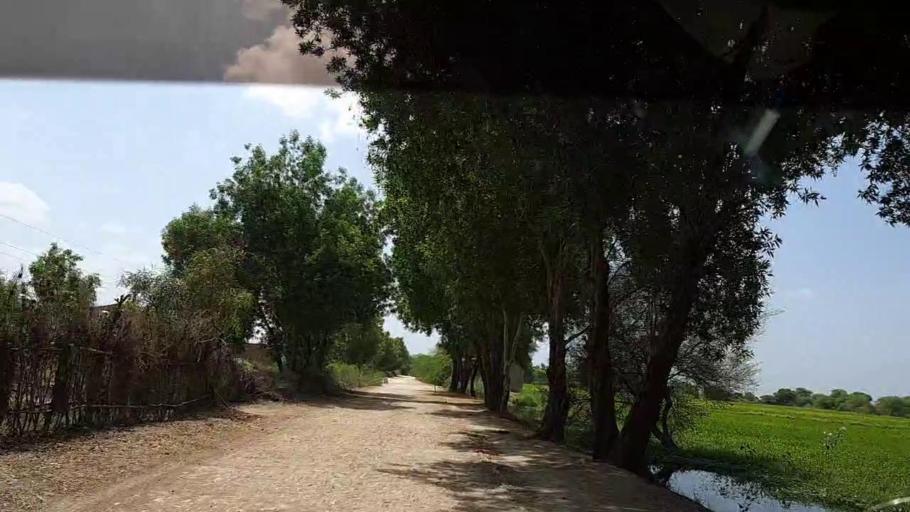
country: PK
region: Sindh
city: Badin
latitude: 24.5709
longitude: 68.7657
